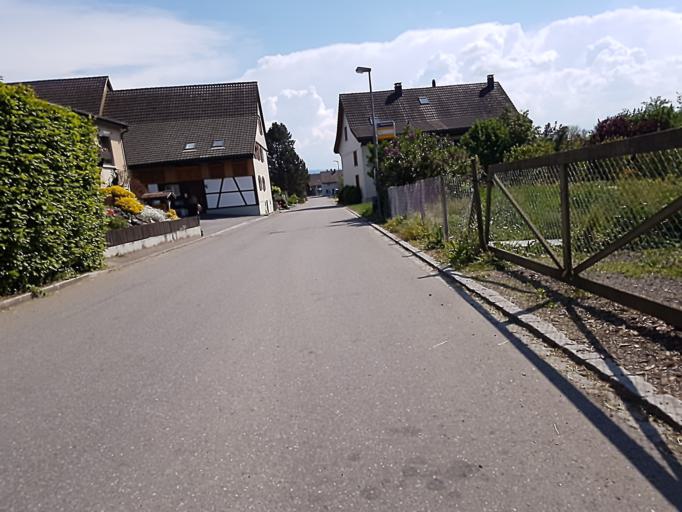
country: CH
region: Thurgau
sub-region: Arbon District
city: Amriswil
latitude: 47.5646
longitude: 9.2988
